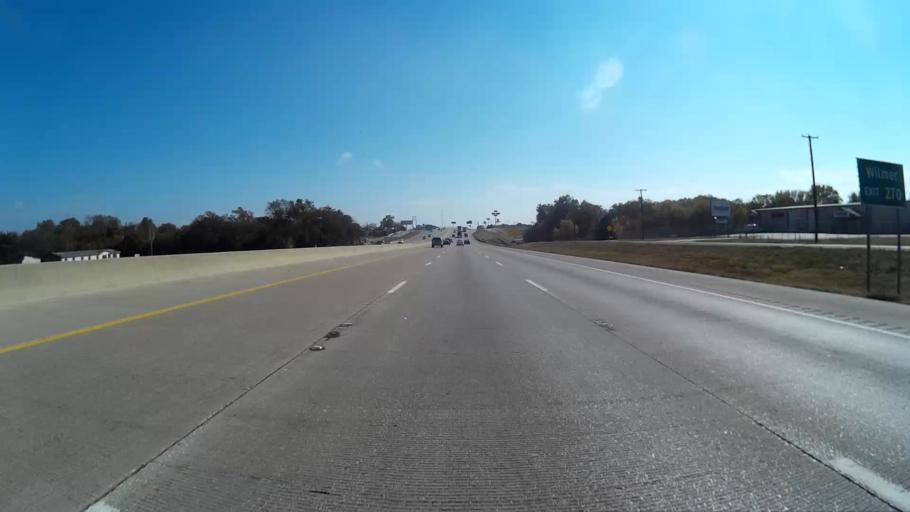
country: US
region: Texas
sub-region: Dallas County
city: Wilmer
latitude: 32.5985
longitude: -96.6832
